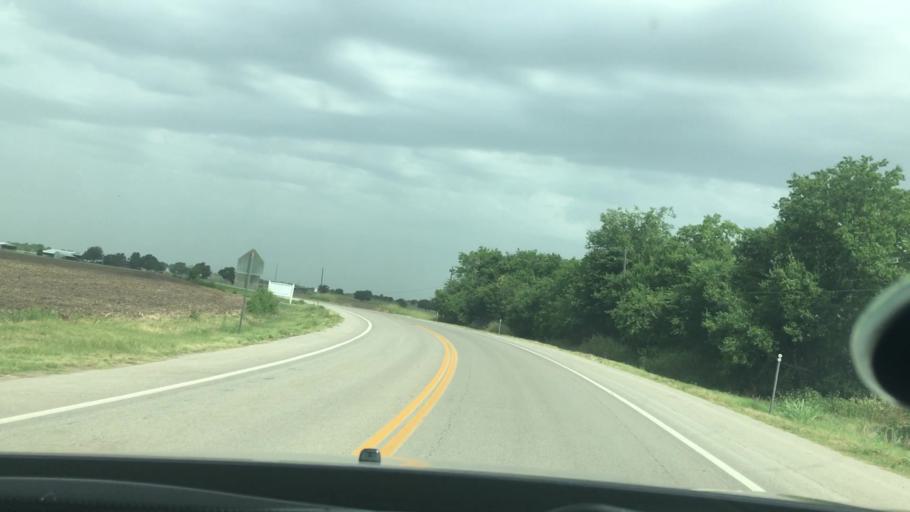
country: US
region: Oklahoma
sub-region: Garvin County
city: Pauls Valley
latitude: 34.8298
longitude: -97.2596
